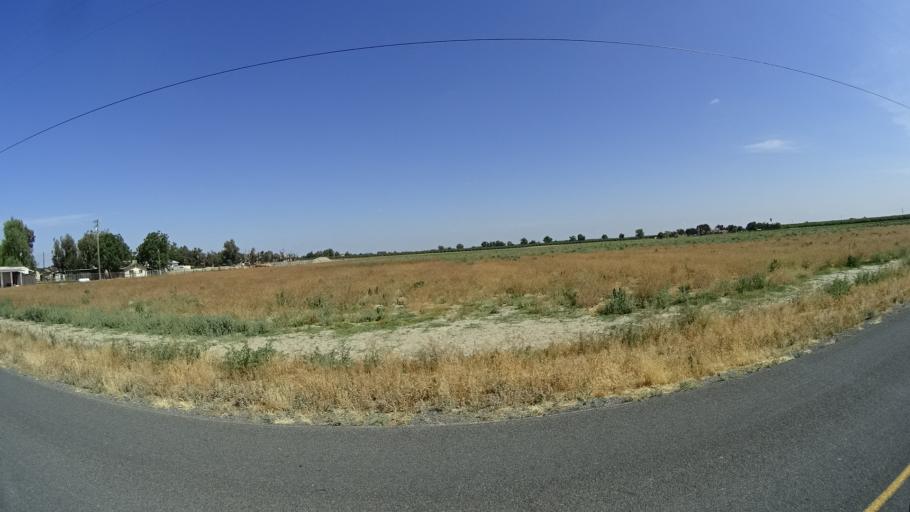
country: US
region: California
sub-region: Kings County
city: Lemoore
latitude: 36.2694
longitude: -119.7409
